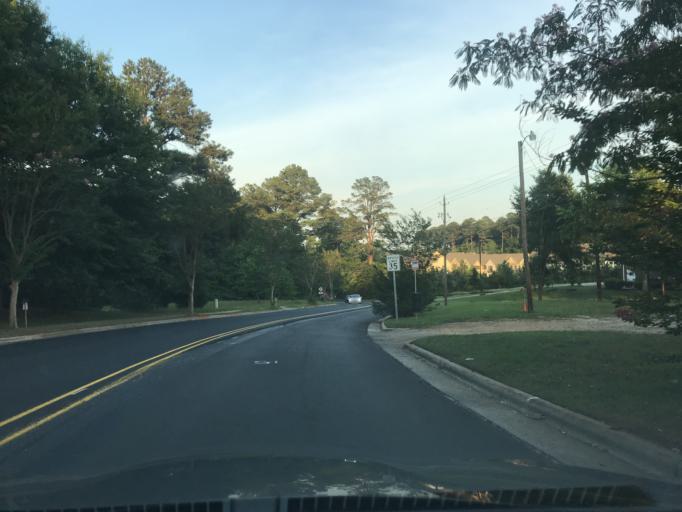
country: US
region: North Carolina
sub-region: Wake County
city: Raleigh
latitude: 35.7404
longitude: -78.6299
